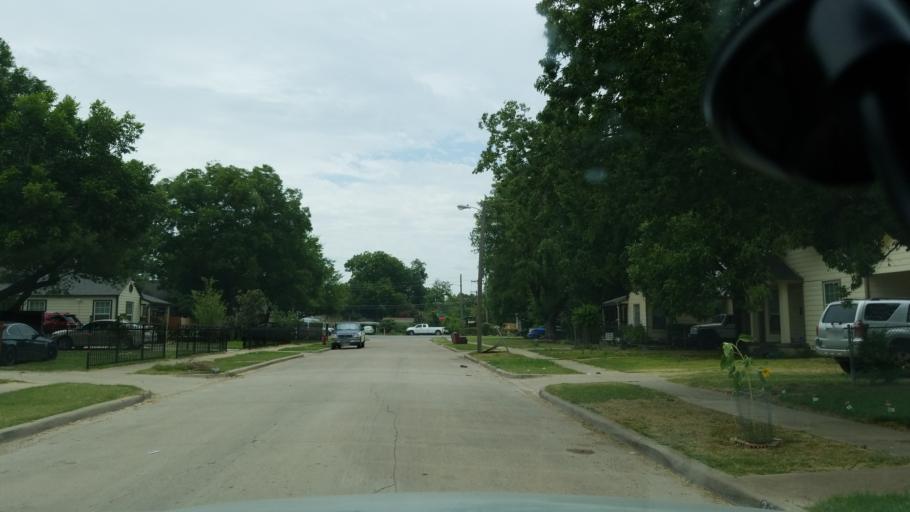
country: US
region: Texas
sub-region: Dallas County
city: Grand Prairie
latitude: 32.7433
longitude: -96.9920
